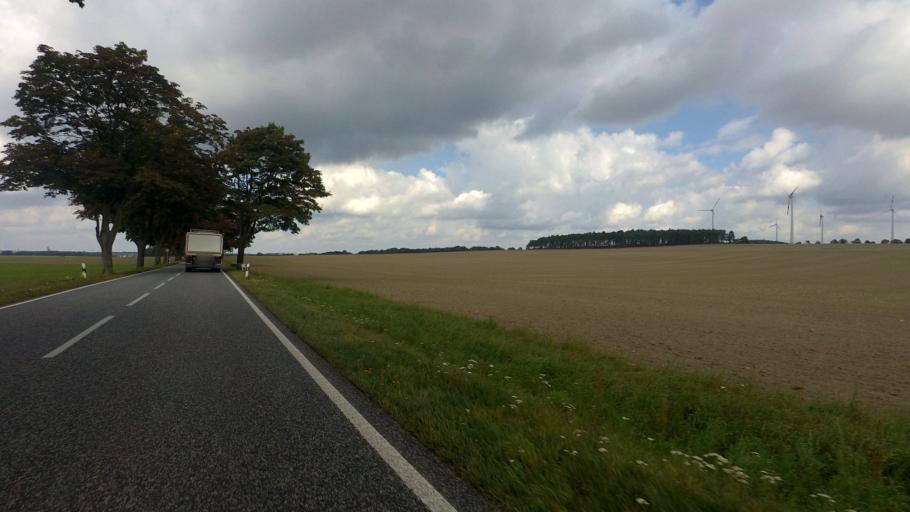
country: DE
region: Brandenburg
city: Juterbog
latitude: 51.9614
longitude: 13.1111
